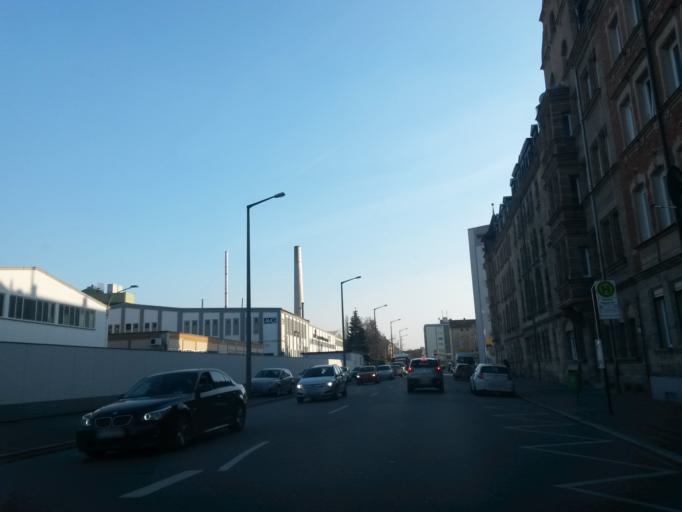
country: DE
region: Bavaria
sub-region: Regierungsbezirk Mittelfranken
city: Furth
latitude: 49.4631
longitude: 11.0110
